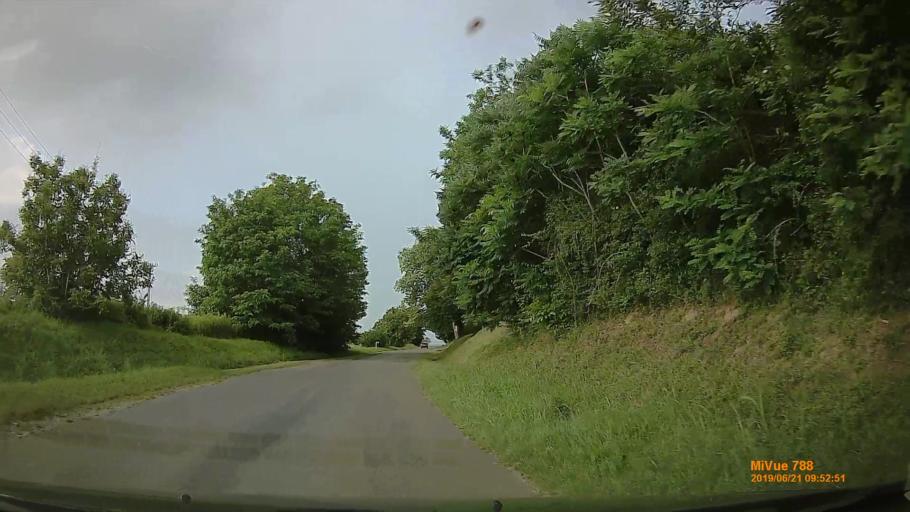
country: HU
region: Baranya
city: Sasd
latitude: 46.2403
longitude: 18.0134
